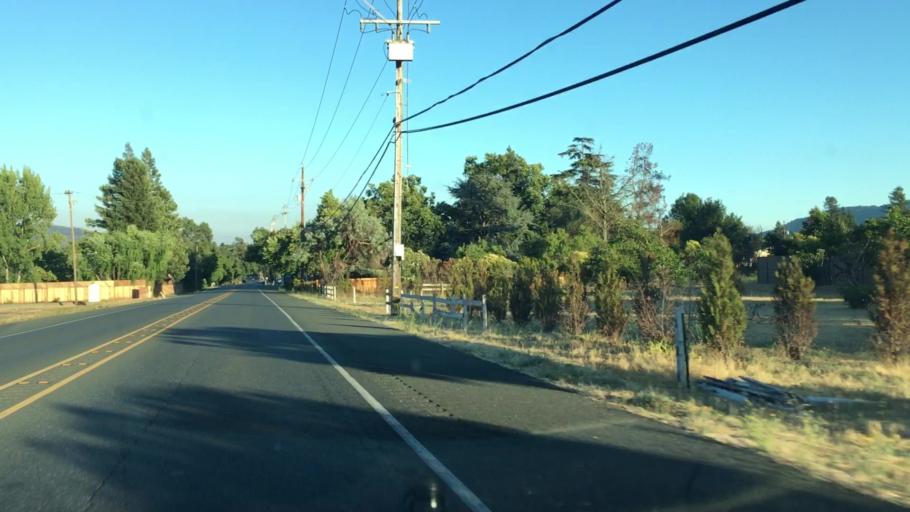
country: US
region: California
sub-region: Sonoma County
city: Kenwood
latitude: 38.4220
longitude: -122.5539
